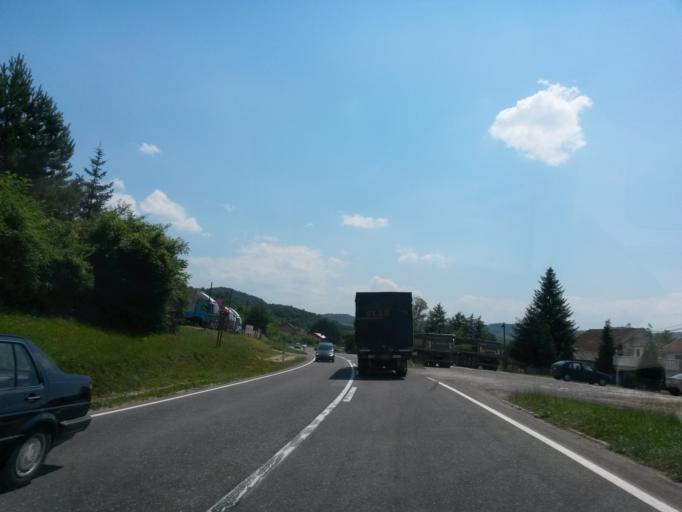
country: BA
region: Federation of Bosnia and Herzegovina
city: Lijesnica
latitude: 44.4946
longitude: 18.0824
